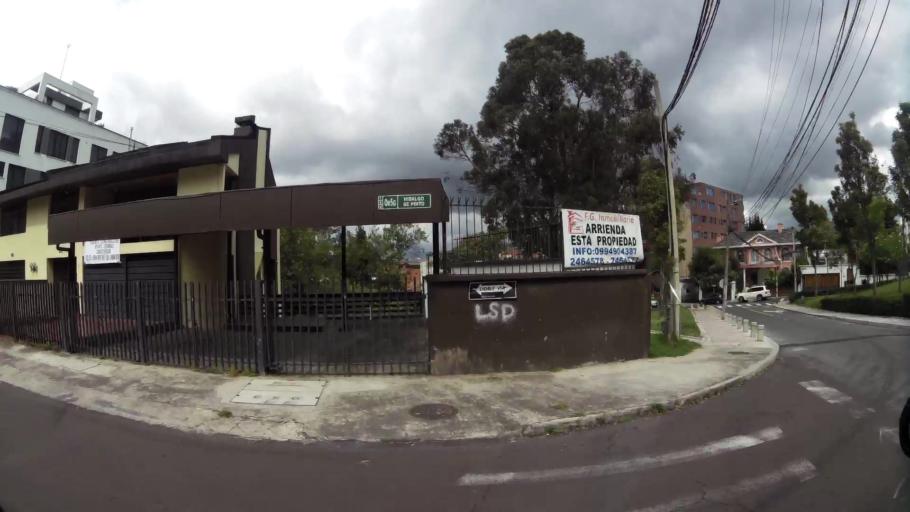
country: EC
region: Pichincha
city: Quito
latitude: -0.1684
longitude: -78.4967
